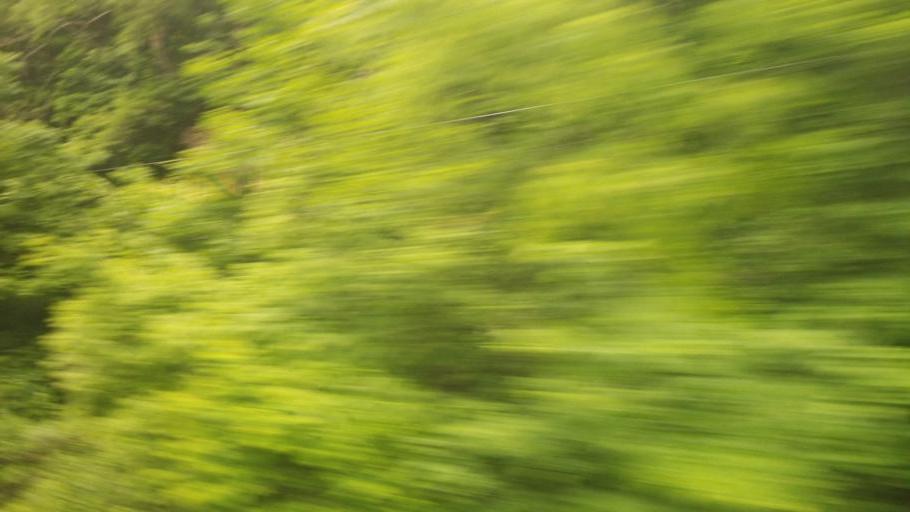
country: US
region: Pennsylvania
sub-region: Somerset County
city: Milford
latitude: 39.8146
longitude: -79.3268
